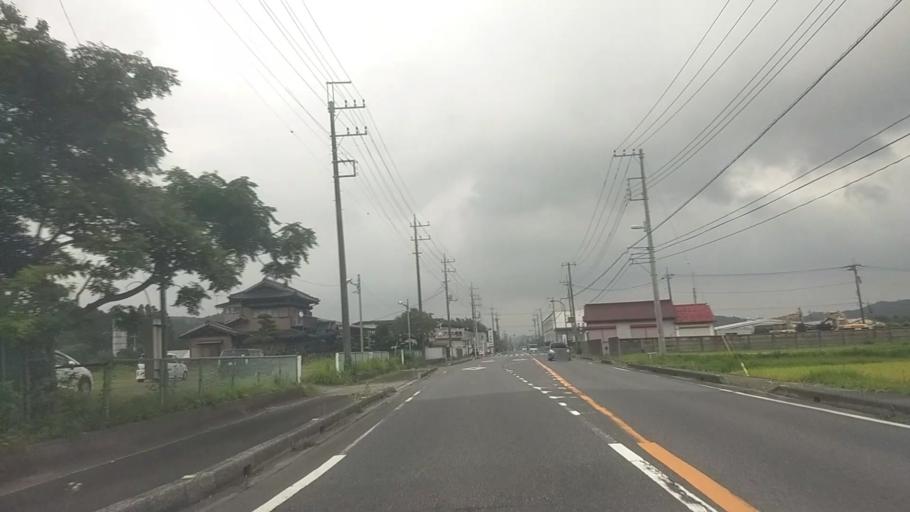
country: JP
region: Chiba
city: Ohara
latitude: 35.2867
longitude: 140.2622
